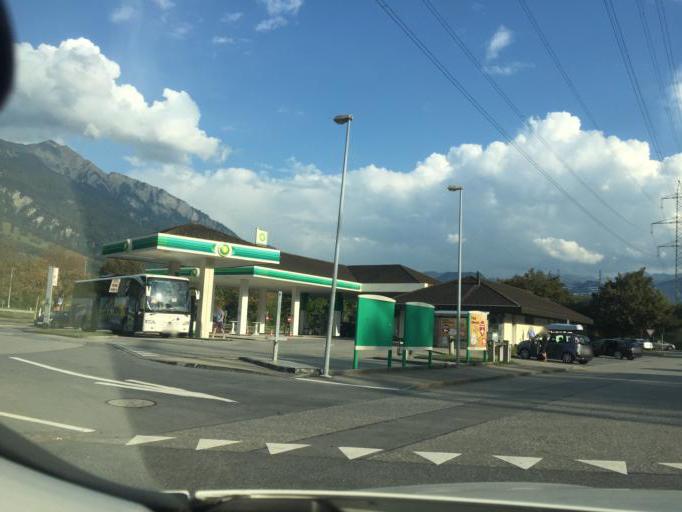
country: CH
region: Saint Gallen
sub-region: Wahlkreis Sarganserland
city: Bad Ragaz
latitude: 47.0114
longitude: 9.5116
